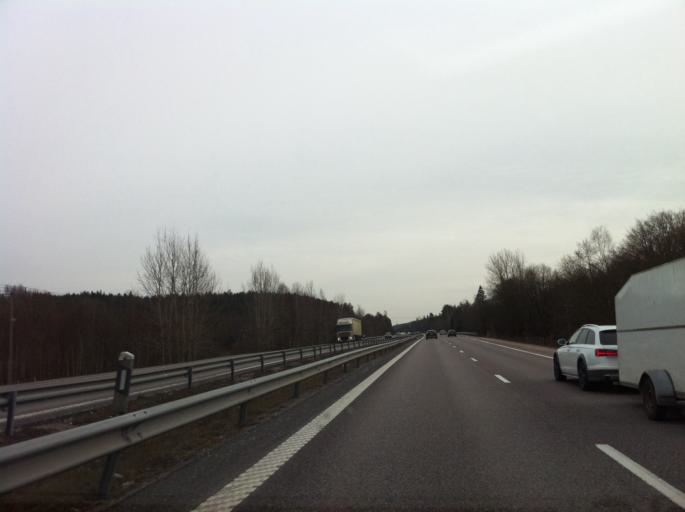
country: SE
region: Vaestra Goetaland
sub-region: Kungalvs Kommun
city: Kode
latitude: 57.9617
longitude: 11.8448
